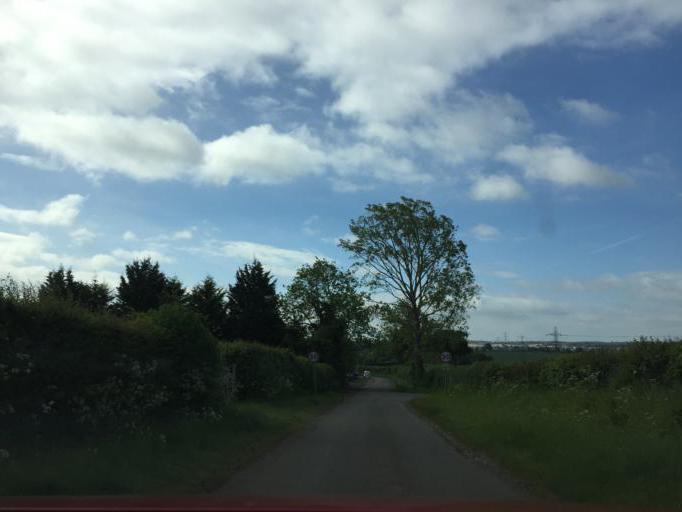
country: GB
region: England
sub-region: Northamptonshire
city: Blisworth
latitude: 52.1449
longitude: -0.9419
